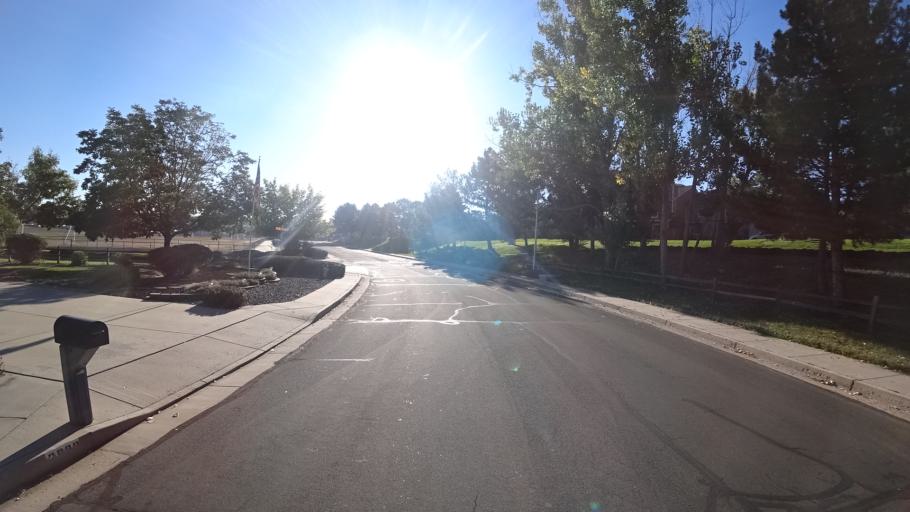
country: US
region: Colorado
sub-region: El Paso County
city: Cimarron Hills
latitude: 38.8863
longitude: -104.7628
